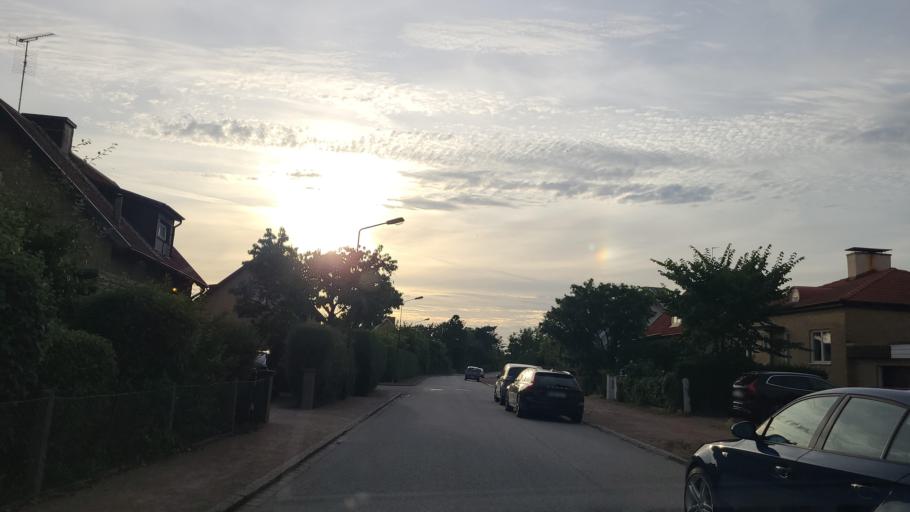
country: SE
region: Skane
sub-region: Malmo
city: Malmoe
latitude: 55.5811
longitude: 12.9636
